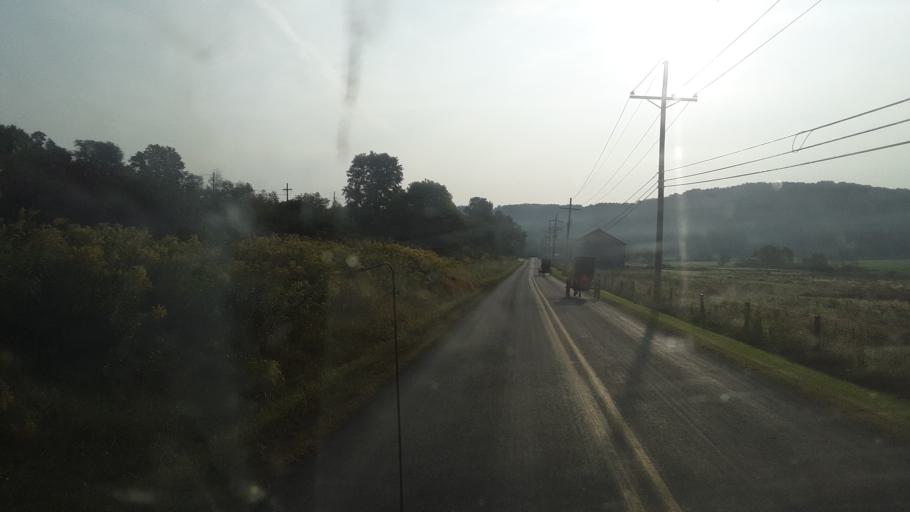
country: US
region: Pennsylvania
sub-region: Jefferson County
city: Punxsutawney
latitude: 40.9661
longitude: -79.1580
